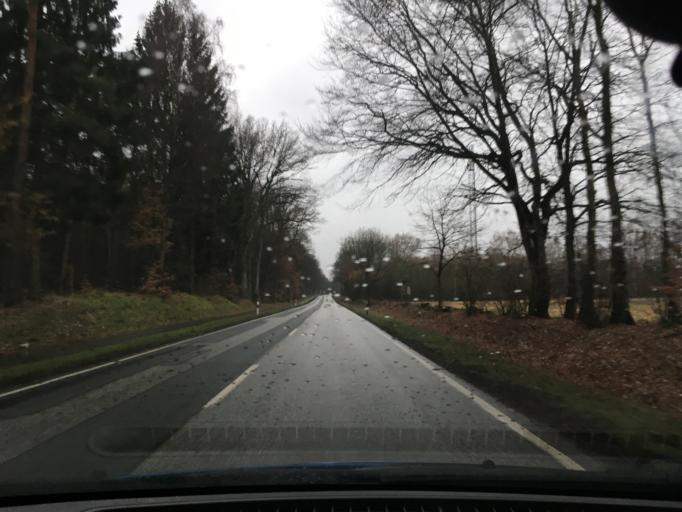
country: DE
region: Schleswig-Holstein
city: Schnakenbek
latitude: 53.3906
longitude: 10.4865
